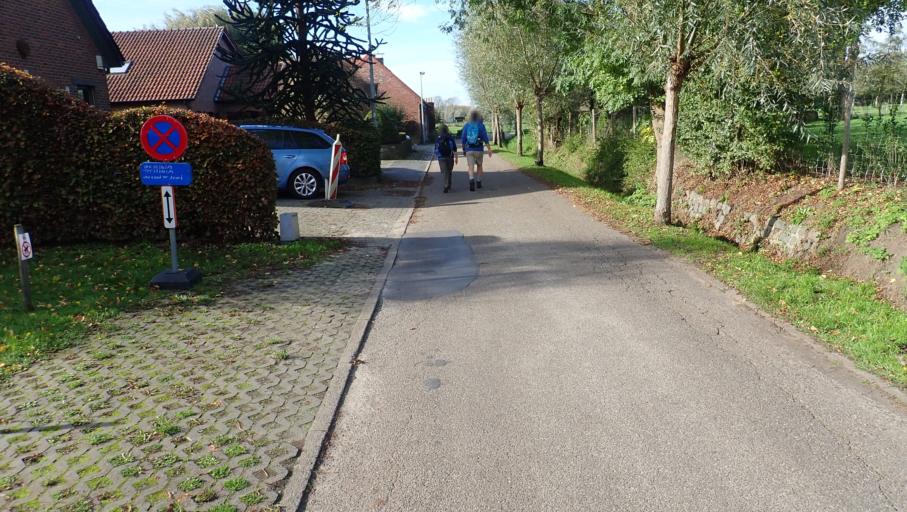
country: BE
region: Flanders
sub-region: Provincie Oost-Vlaanderen
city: Stekene
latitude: 51.1596
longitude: 4.0409
